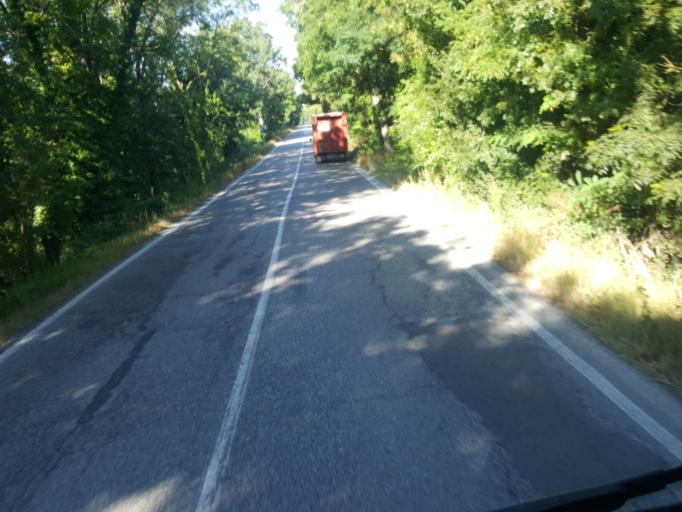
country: IT
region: The Marches
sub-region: Provincia di Pesaro e Urbino
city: Montecalvo in Foglia
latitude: 43.7921
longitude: 12.6459
